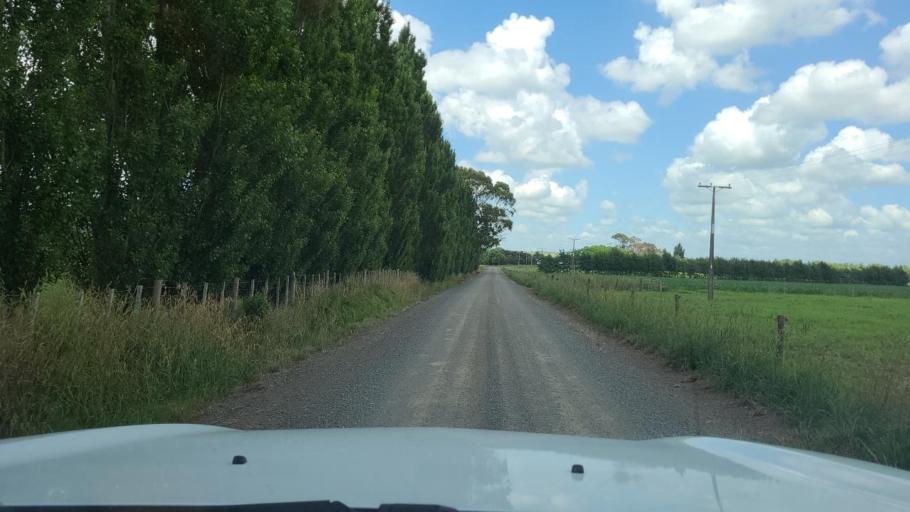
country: NZ
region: Waikato
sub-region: Hauraki District
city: Ngatea
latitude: -37.5080
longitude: 175.4410
